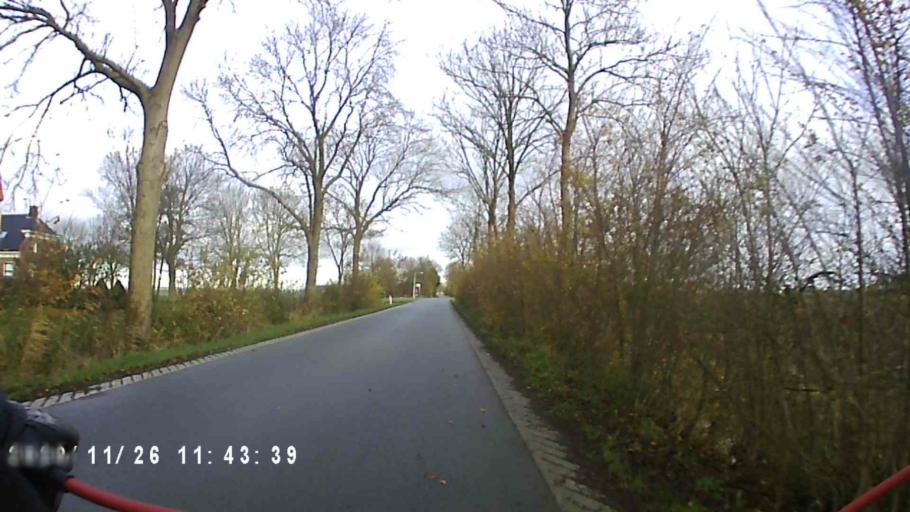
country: NL
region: Groningen
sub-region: Gemeente Bedum
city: Bedum
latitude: 53.2991
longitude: 6.5749
